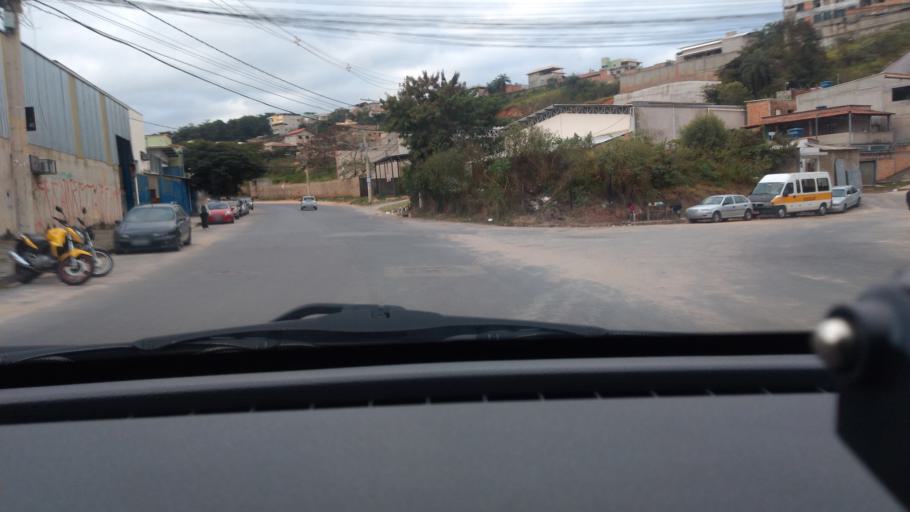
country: BR
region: Minas Gerais
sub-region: Santa Luzia
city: Santa Luzia
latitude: -19.8184
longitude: -43.9375
